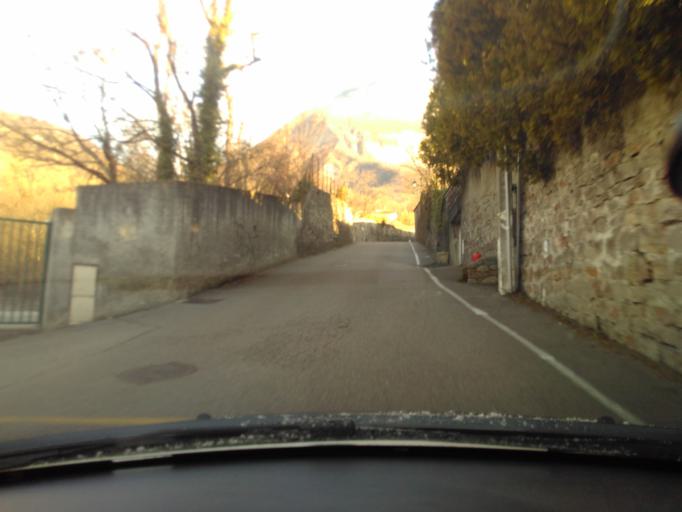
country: FR
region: Rhone-Alpes
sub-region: Departement de l'Isere
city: Corenc
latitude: 45.2144
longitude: 5.7530
